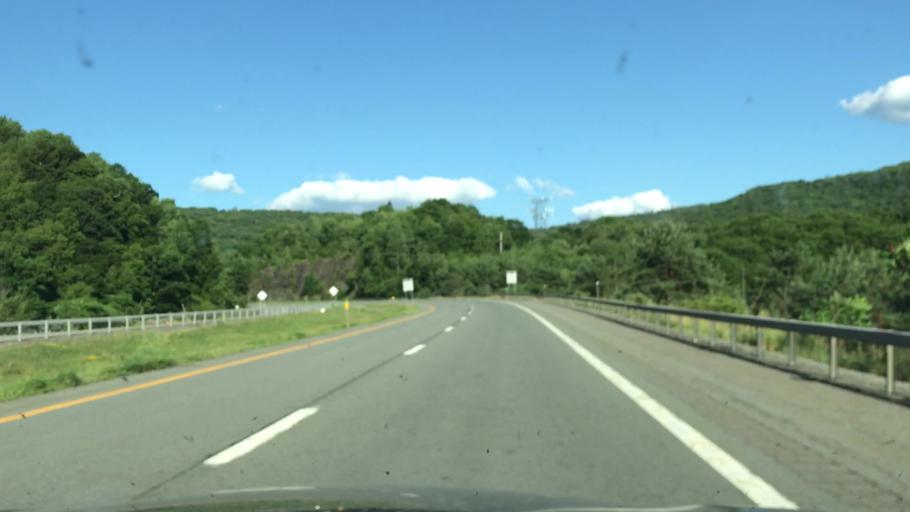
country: US
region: New York
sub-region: Sullivan County
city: Livingston Manor
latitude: 41.9498
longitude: -74.9645
